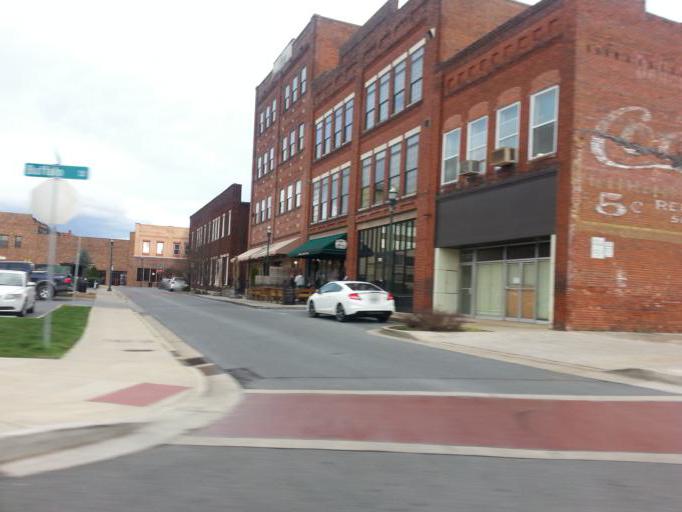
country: US
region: Tennessee
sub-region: Washington County
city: Johnson City
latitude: 36.3154
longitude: -82.3528
